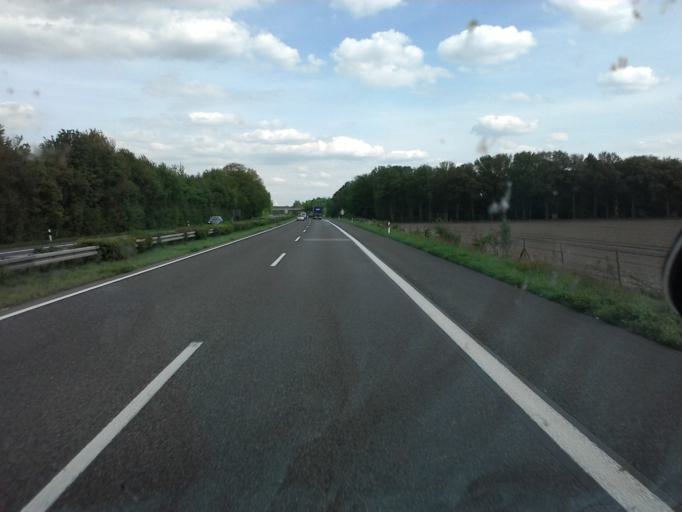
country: DE
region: North Rhine-Westphalia
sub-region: Regierungsbezirk Dusseldorf
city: Issum
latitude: 51.5682
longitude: 6.4575
